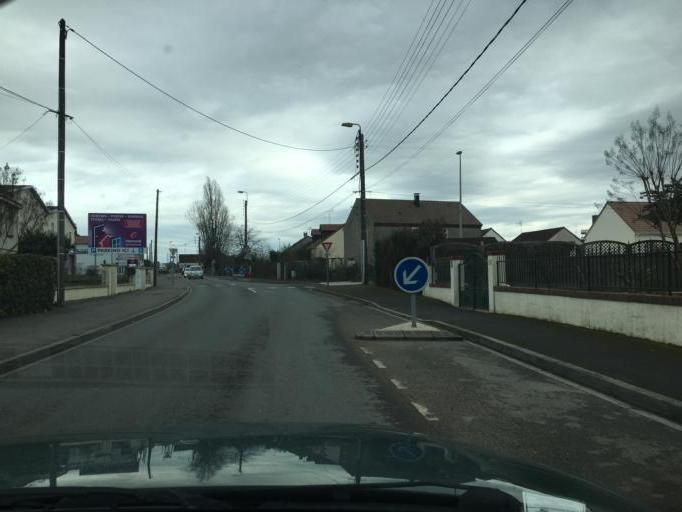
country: FR
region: Centre
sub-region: Departement du Loiret
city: Fleury-les-Aubrais
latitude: 47.9460
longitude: 1.9057
